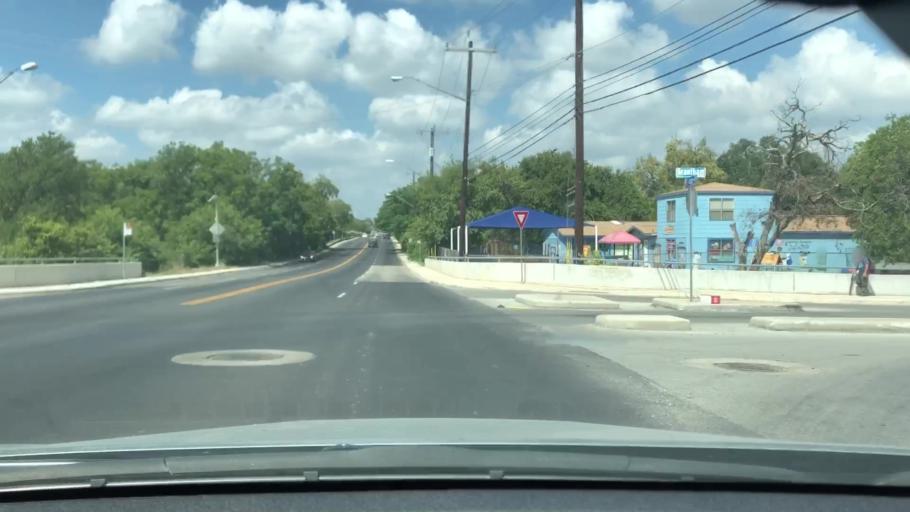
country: US
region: Texas
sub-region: Bexar County
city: Terrell Hills
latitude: 29.4849
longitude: -98.4180
